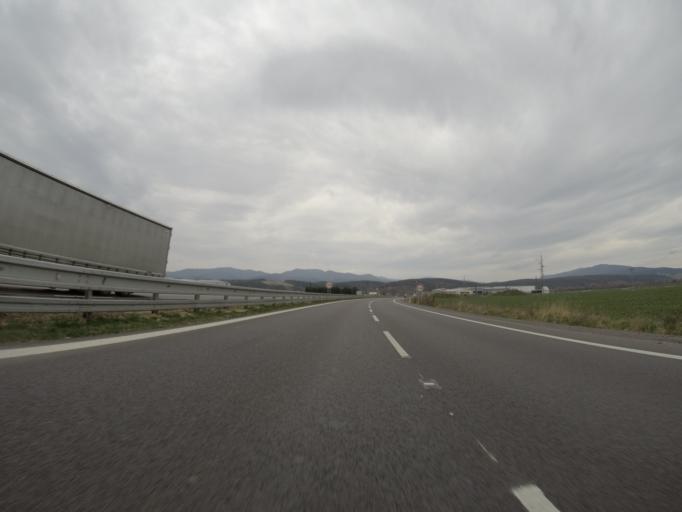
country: SK
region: Nitriansky
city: Novaky
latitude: 48.7215
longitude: 18.5580
